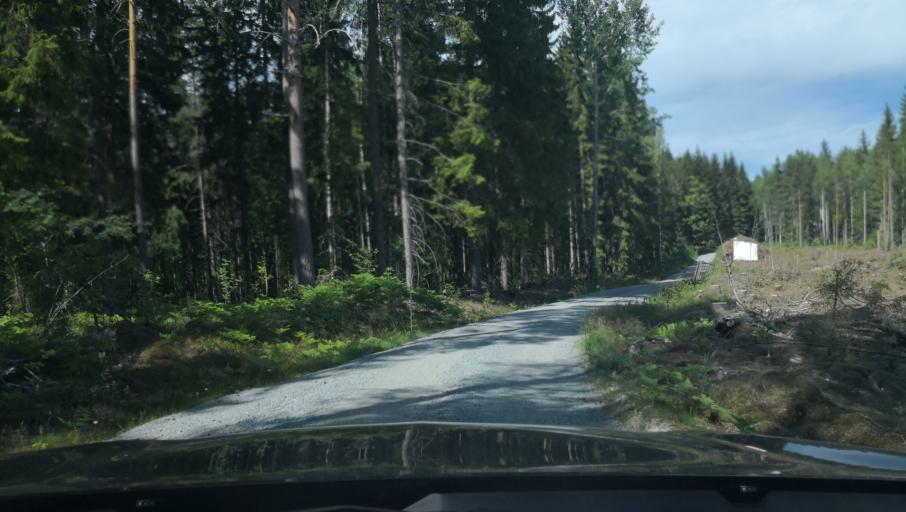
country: SE
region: Vaestmanland
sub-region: Surahammars Kommun
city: Ramnas
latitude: 59.9439
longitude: 16.1900
